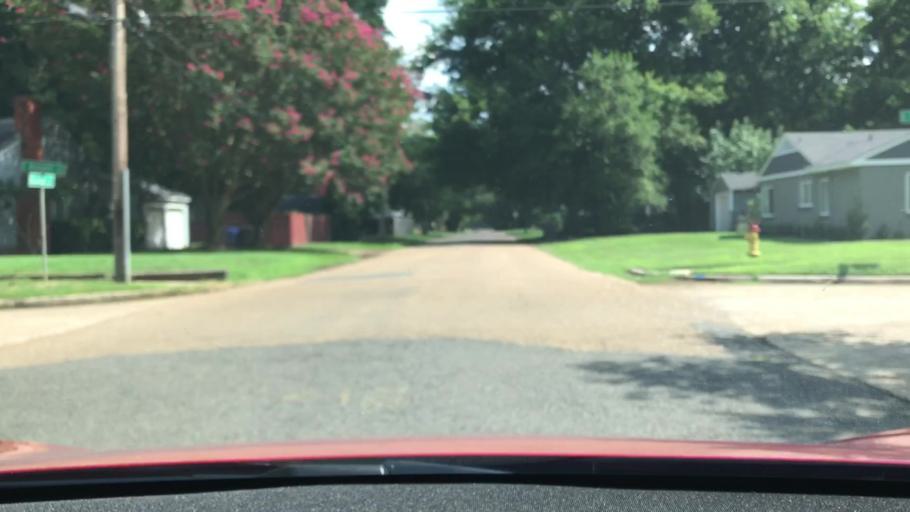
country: US
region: Louisiana
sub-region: Bossier Parish
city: Bossier City
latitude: 32.4746
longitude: -93.7313
